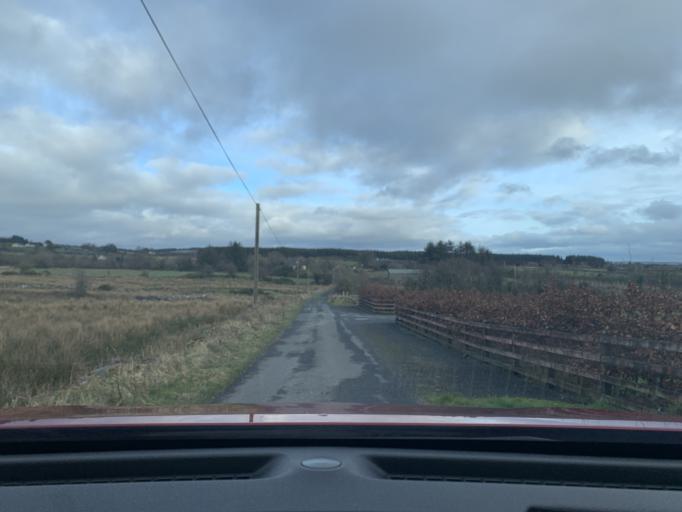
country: IE
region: Connaught
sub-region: Roscommon
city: Ballaghaderreen
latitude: 53.9348
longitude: -8.5444
